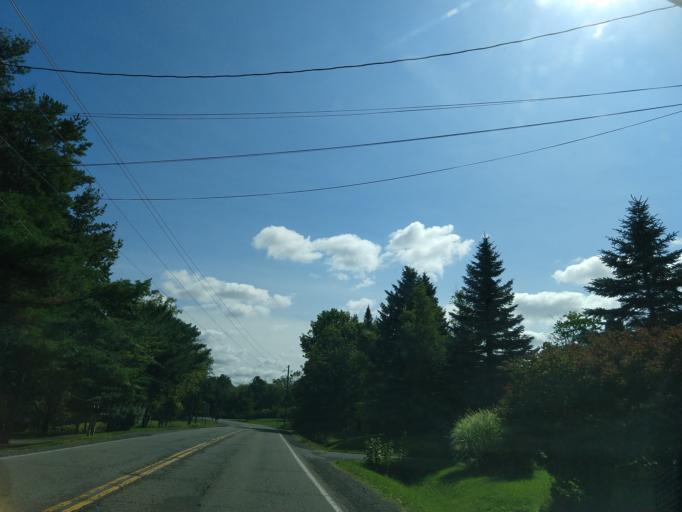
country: US
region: New York
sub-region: Tompkins County
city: South Hill
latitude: 42.4216
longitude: -76.4841
